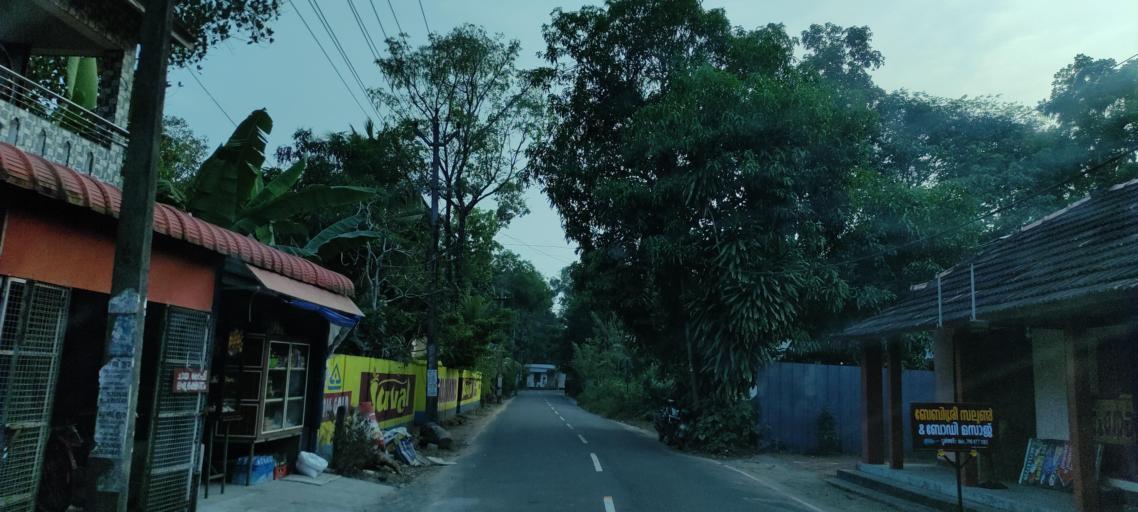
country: IN
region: Kerala
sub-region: Alappuzha
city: Mavelikara
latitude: 9.2787
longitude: 76.5538
